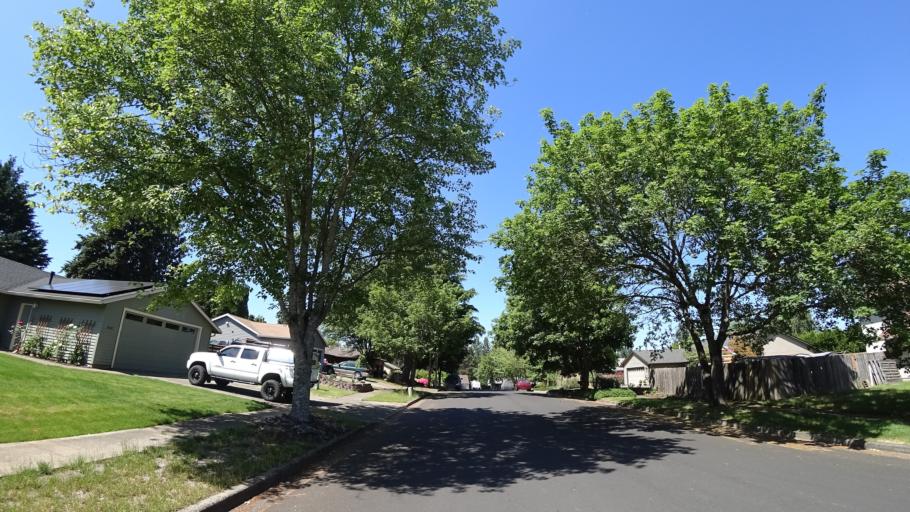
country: US
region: Oregon
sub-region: Washington County
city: Tigard
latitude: 45.4446
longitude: -122.8096
